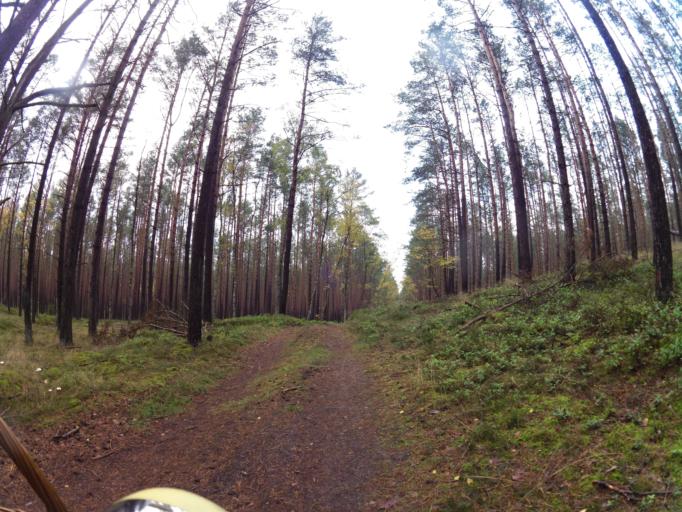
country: PL
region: West Pomeranian Voivodeship
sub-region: Powiat policki
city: Nowe Warpno
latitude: 53.6171
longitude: 14.3451
